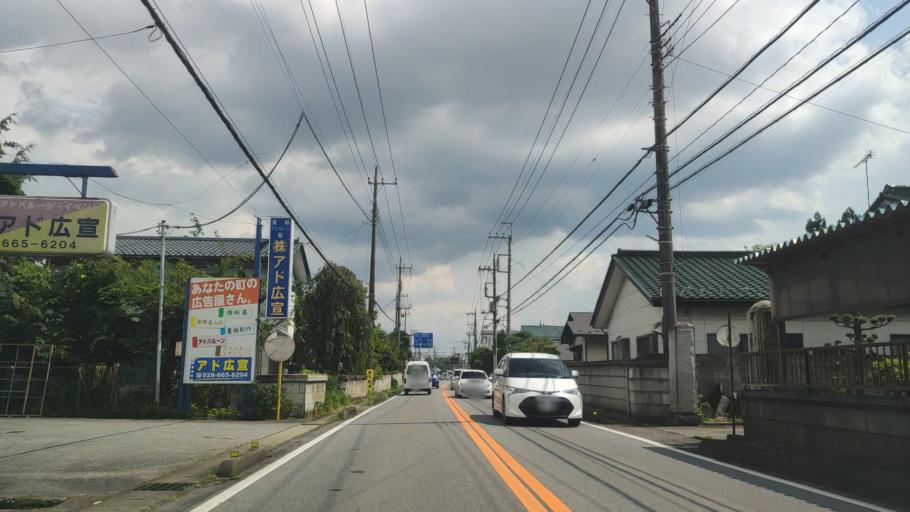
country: JP
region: Tochigi
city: Utsunomiya-shi
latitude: 36.6516
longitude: 139.8431
